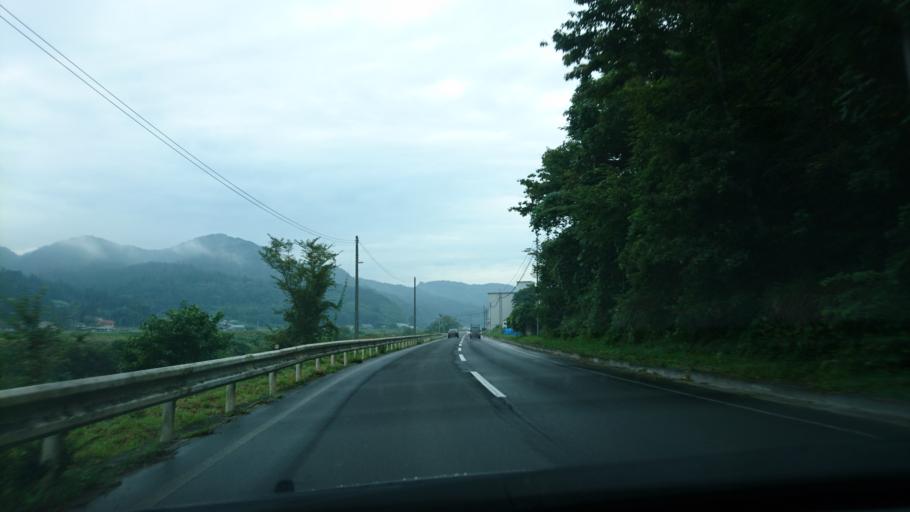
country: JP
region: Iwate
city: Ichinoseki
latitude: 38.9632
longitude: 141.2458
